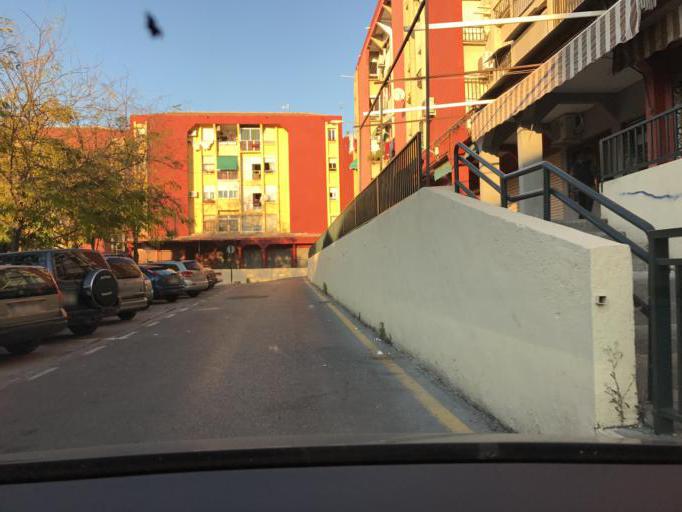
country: ES
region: Andalusia
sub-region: Provincia de Granada
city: Granada
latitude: 37.1994
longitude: -3.5978
